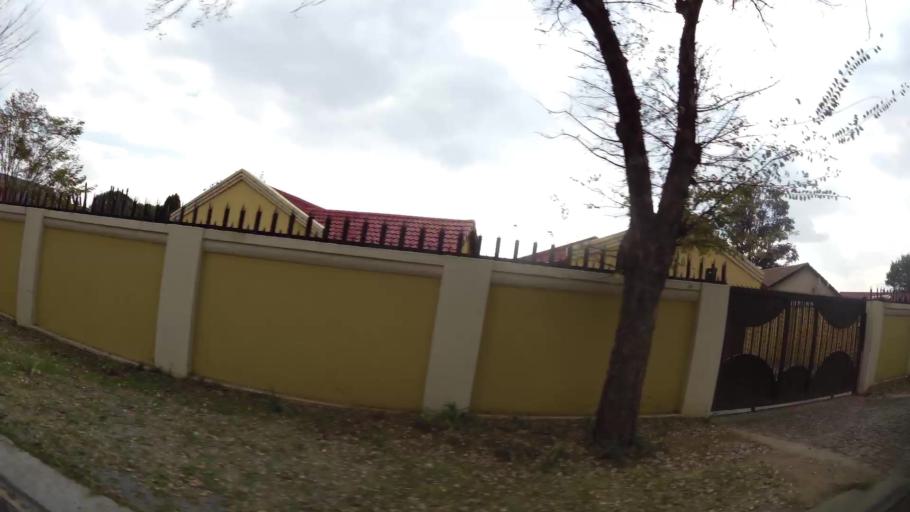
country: ZA
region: Gauteng
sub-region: Ekurhuleni Metropolitan Municipality
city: Benoni
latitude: -26.1254
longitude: 28.3621
